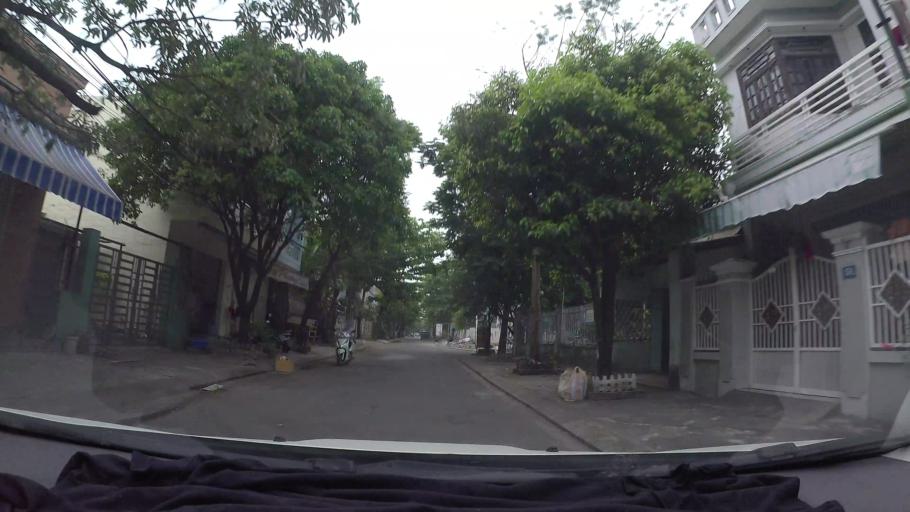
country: VN
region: Da Nang
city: Thanh Khe
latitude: 16.0530
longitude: 108.1789
